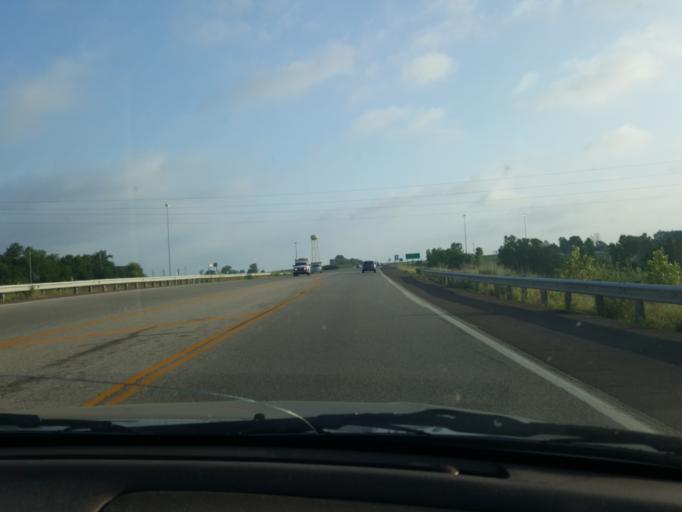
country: US
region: Kansas
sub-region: Douglas County
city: Lawrence
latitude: 38.9925
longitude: -95.3436
